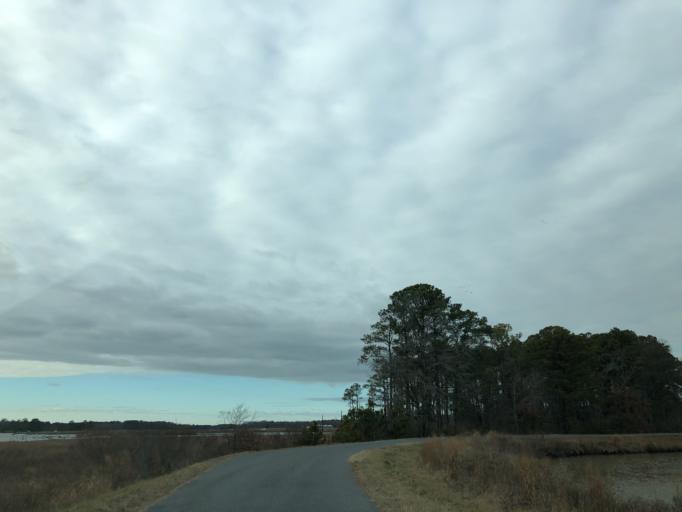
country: US
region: Maryland
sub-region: Dorchester County
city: Cambridge
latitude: 38.4407
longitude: -76.1221
